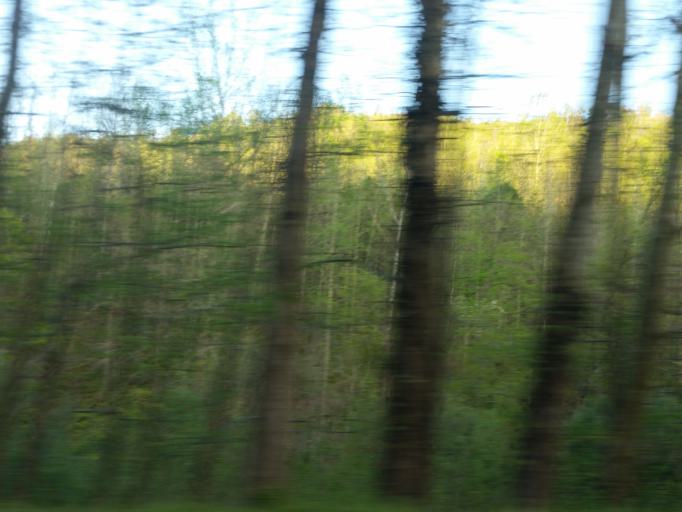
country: US
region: Kentucky
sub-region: Bell County
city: Middlesboro
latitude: 36.5825
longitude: -83.9056
